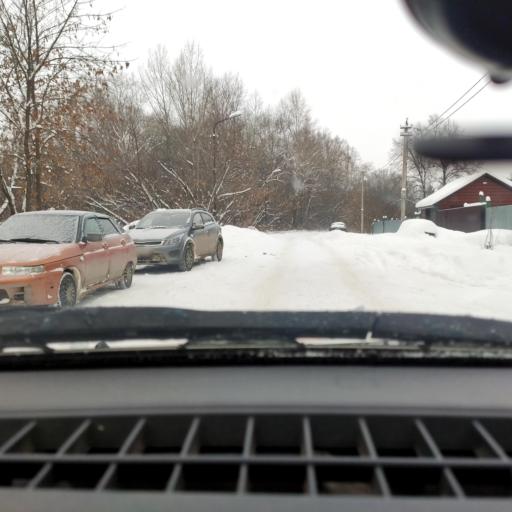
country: RU
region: Bashkortostan
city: Ufa
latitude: 54.7196
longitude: 55.9183
